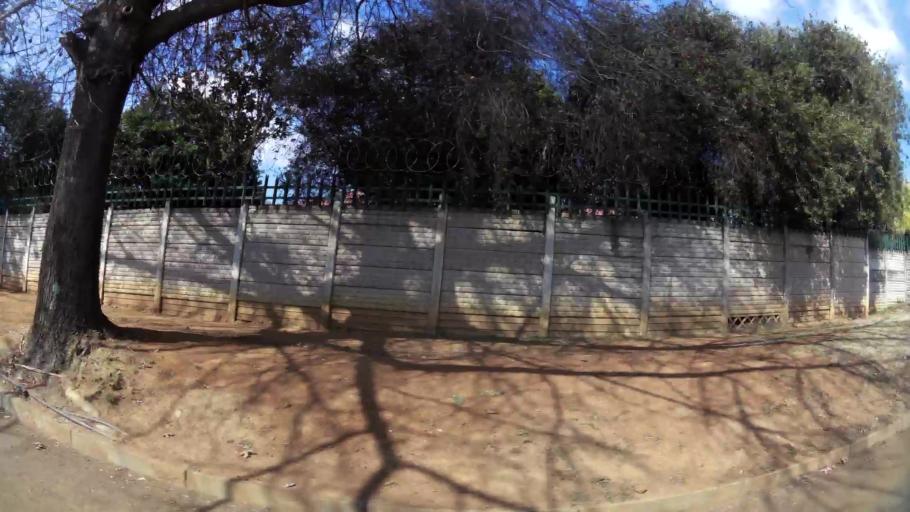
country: ZA
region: Gauteng
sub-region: City of Johannesburg Metropolitan Municipality
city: Modderfontein
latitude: -26.0731
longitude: 28.2336
